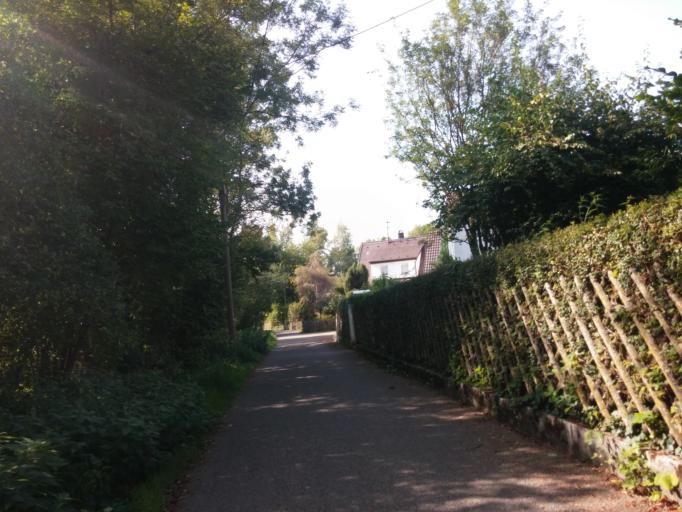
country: DE
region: Bavaria
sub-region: Swabia
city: Benningen
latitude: 47.9729
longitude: 10.2012
